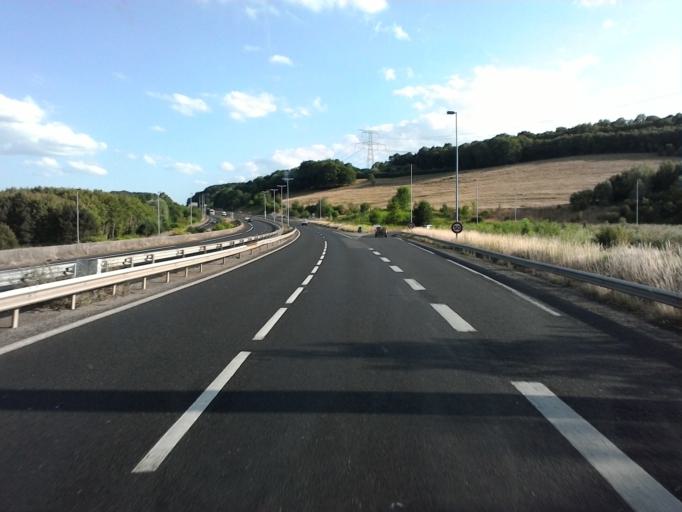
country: FR
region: Lorraine
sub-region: Departement de Meurthe-et-Moselle
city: Flavigny-sur-Moselle
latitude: 48.5776
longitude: 6.1747
